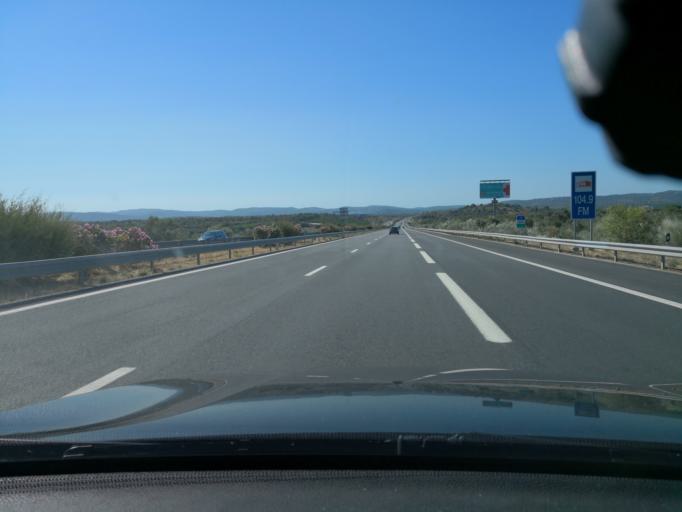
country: PT
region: Faro
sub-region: Silves
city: Sao Bartolomeu de Messines
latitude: 37.2374
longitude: -8.2537
